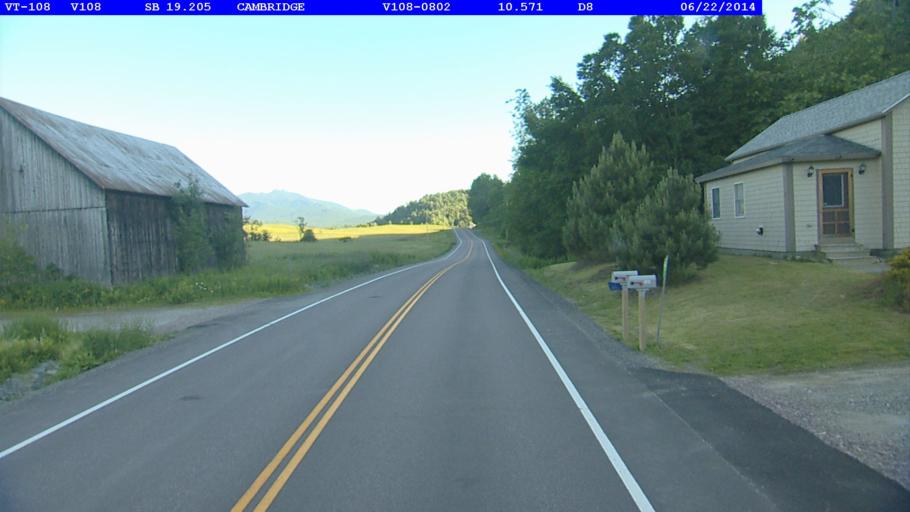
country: US
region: Vermont
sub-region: Lamoille County
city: Johnson
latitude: 44.6679
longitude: -72.8283
